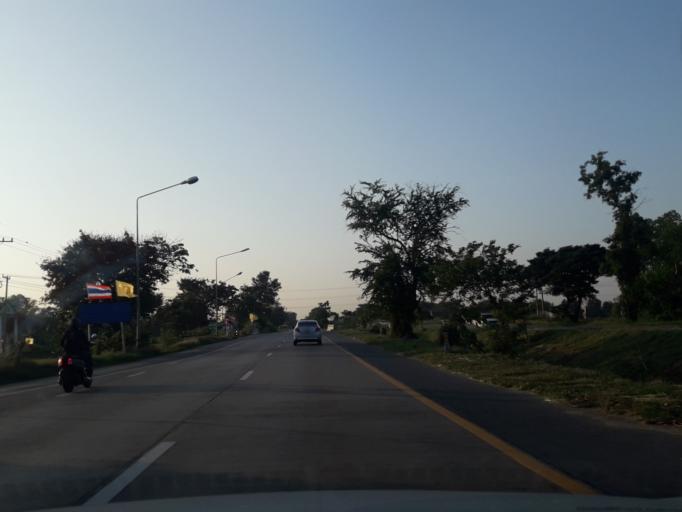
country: TH
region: Phra Nakhon Si Ayutthaya
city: Bang Pa-in
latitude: 14.2778
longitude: 100.5288
